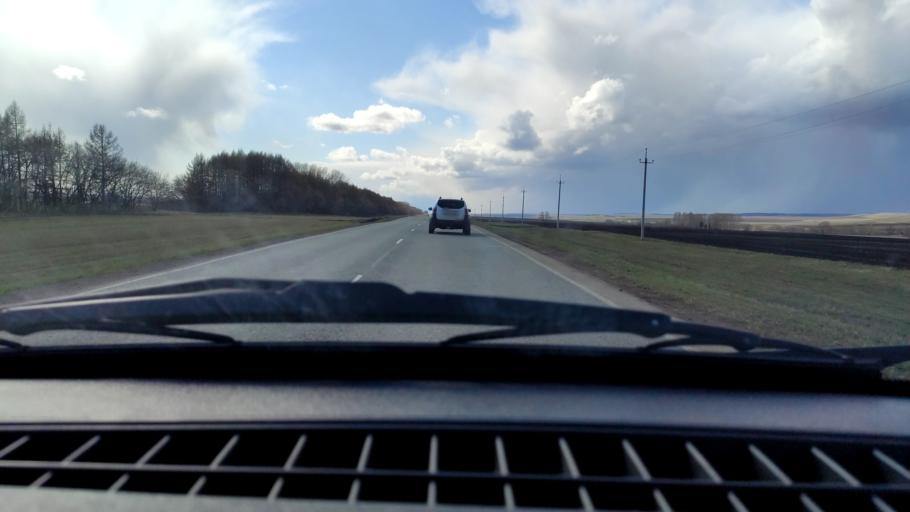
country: RU
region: Bashkortostan
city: Chekmagush
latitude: 55.1112
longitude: 54.9197
